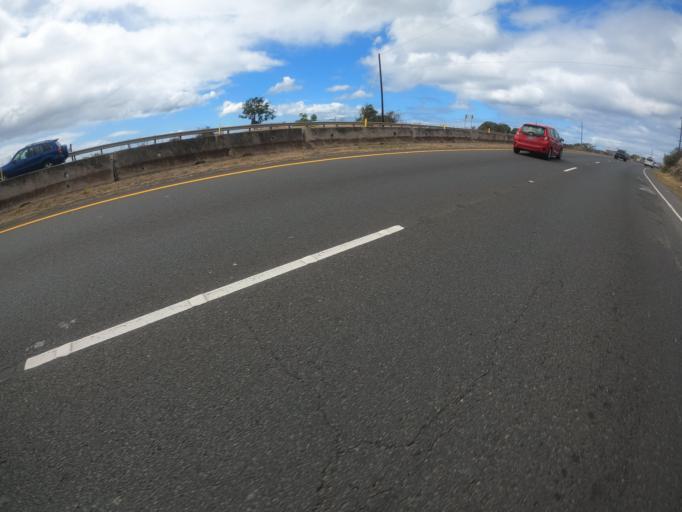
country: US
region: Hawaii
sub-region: Honolulu County
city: Makakilo City
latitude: 21.3421
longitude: -158.1091
